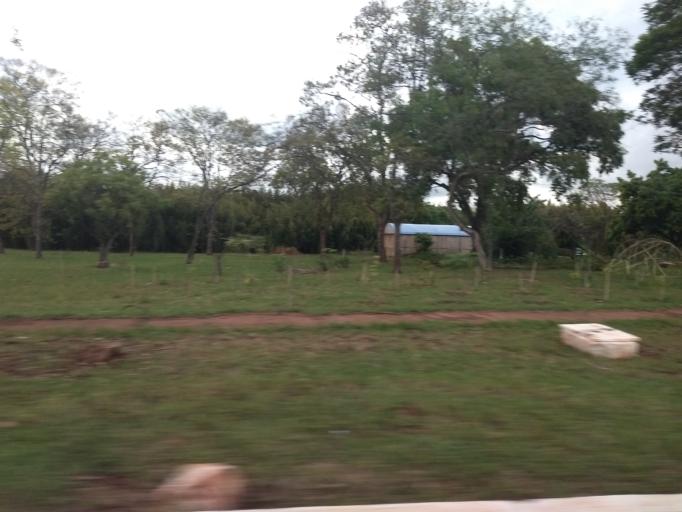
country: BR
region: Federal District
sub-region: Brasilia
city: Brasilia
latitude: -15.7906
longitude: -47.9038
